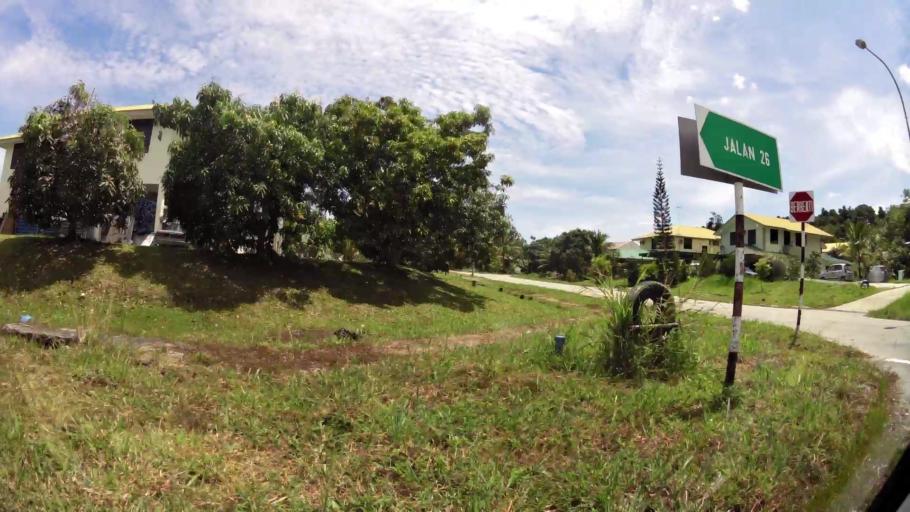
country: BN
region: Brunei and Muara
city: Bandar Seri Begawan
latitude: 4.9585
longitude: 114.9066
